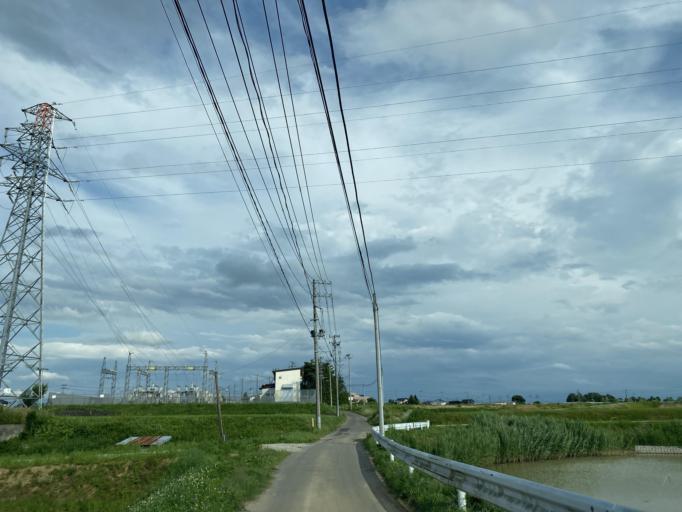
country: JP
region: Fukushima
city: Sukagawa
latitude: 37.3082
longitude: 140.3541
